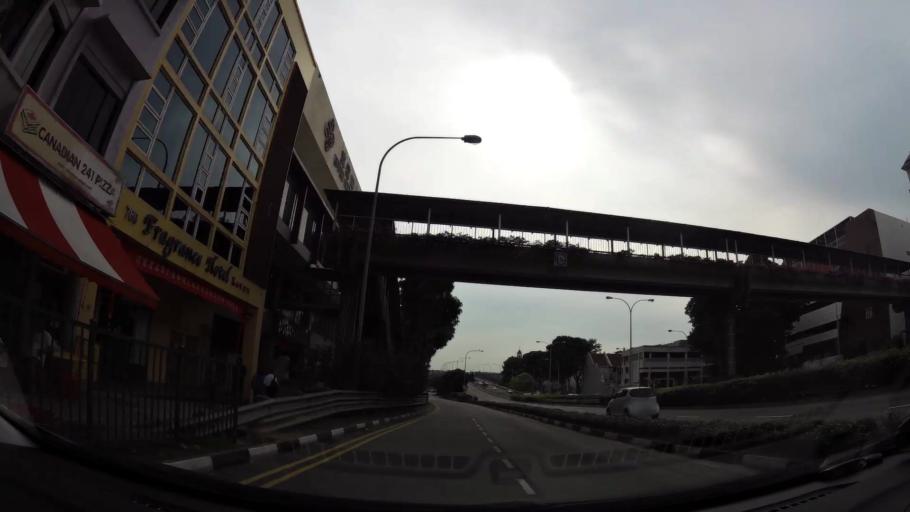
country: SG
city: Singapore
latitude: 1.3542
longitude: 103.8786
